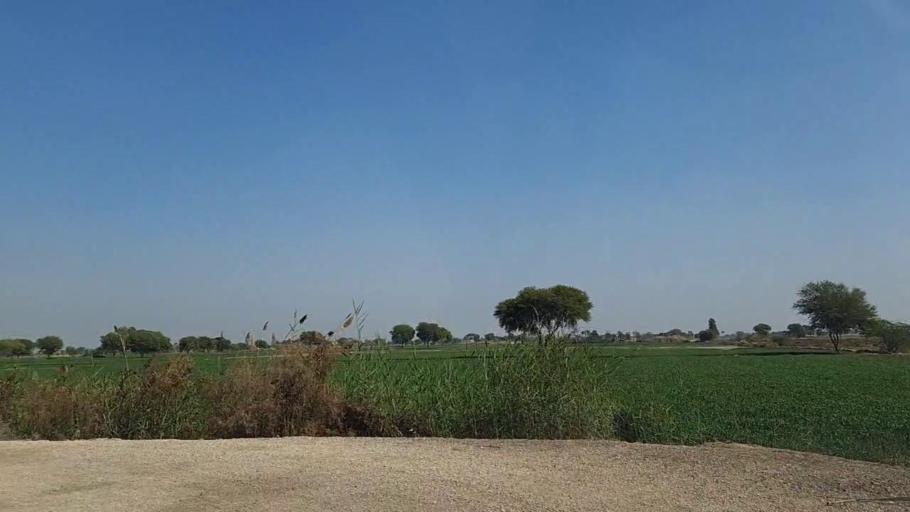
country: PK
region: Sindh
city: Daur
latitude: 26.3596
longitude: 68.3379
